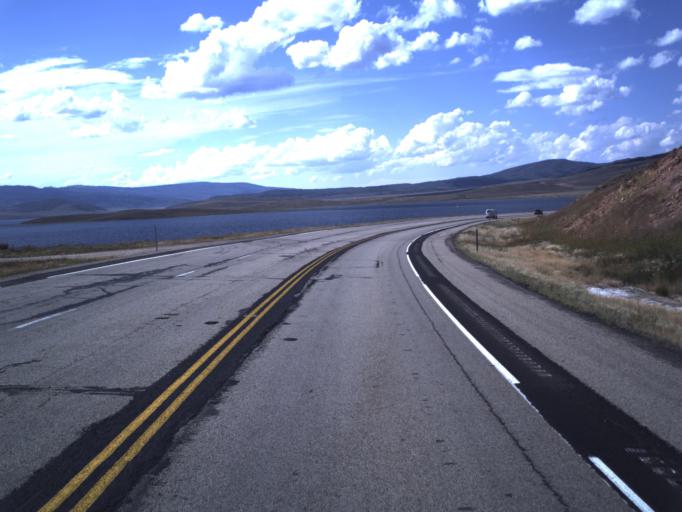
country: US
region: Utah
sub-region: Wasatch County
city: Heber
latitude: 40.1985
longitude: -111.1031
